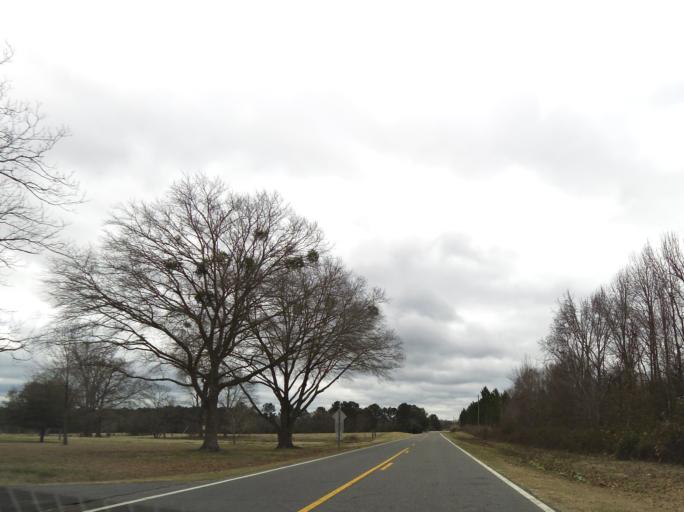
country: US
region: Georgia
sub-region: Bleckley County
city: Cochran
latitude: 32.4628
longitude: -83.3808
